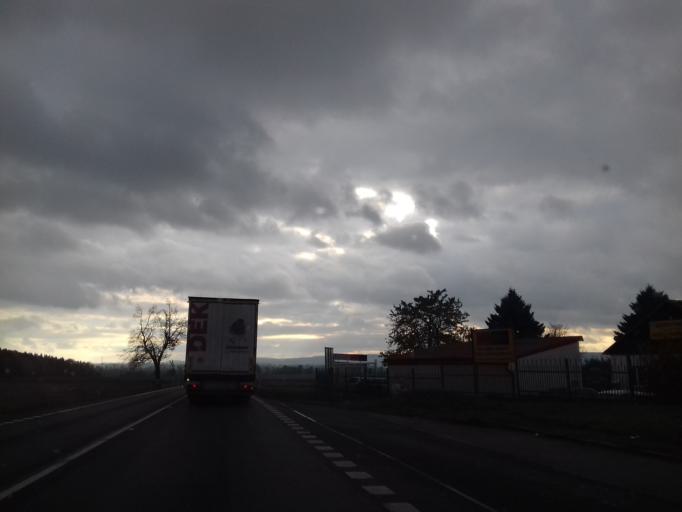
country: CZ
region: Pardubicky
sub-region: Okres Svitavy
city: Svitavy
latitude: 49.7687
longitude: 16.5170
